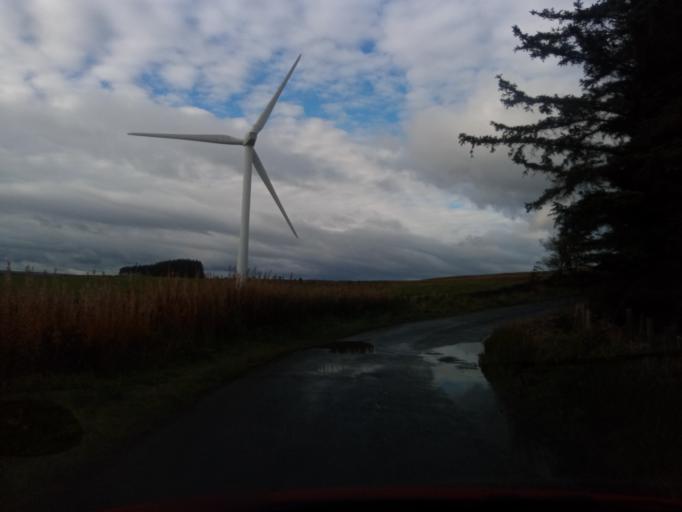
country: GB
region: Scotland
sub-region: The Scottish Borders
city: Galashiels
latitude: 55.6886
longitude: -2.8545
